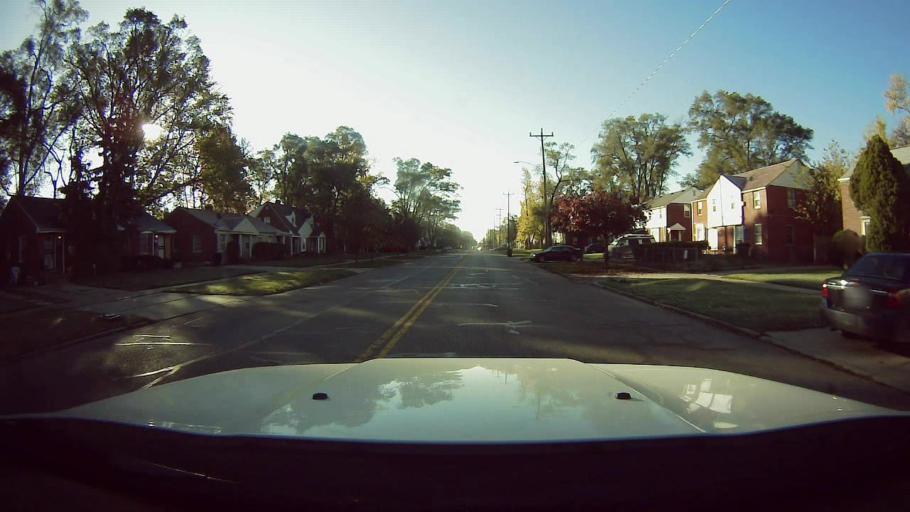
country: US
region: Michigan
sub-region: Oakland County
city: Oak Park
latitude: 42.4423
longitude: -83.1711
